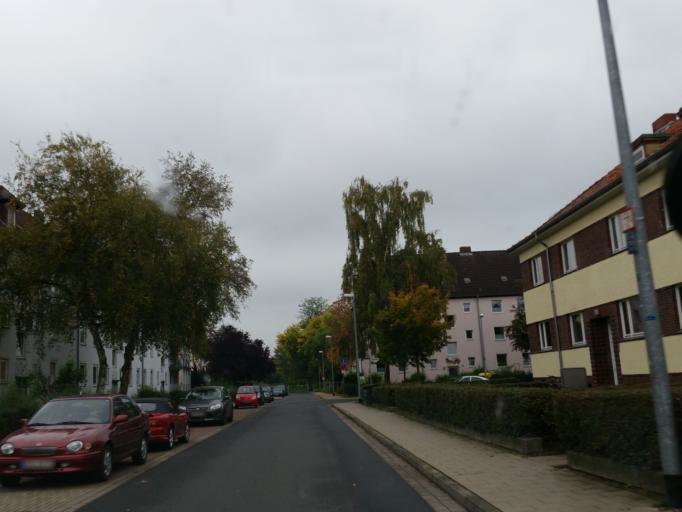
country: DE
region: Lower Saxony
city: Braunschweig
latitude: 52.2451
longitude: 10.5429
